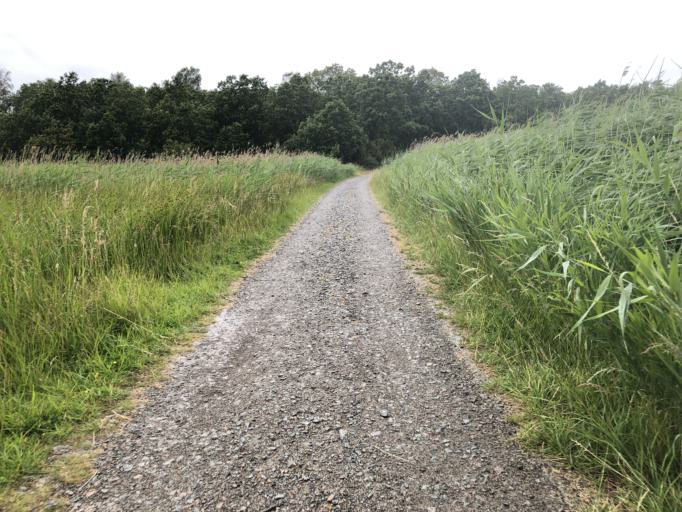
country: SE
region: Kalmar
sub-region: Kalmar Kommun
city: Kalmar
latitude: 56.6374
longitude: 16.3217
